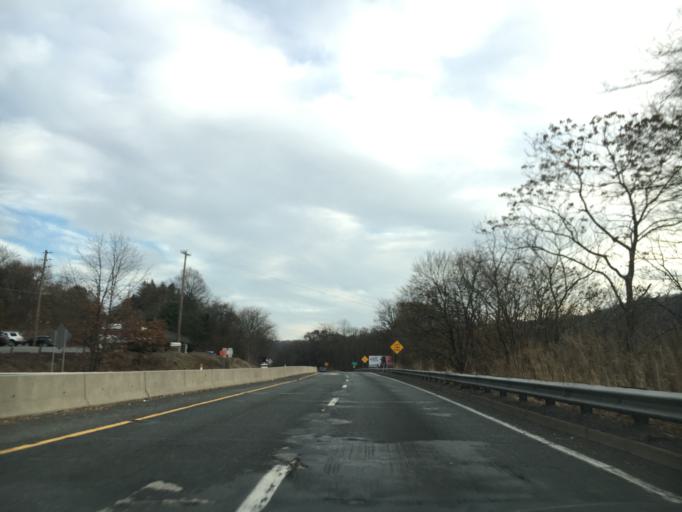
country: US
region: Pennsylvania
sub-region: Carbon County
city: Weissport East
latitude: 40.8272
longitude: -75.6976
